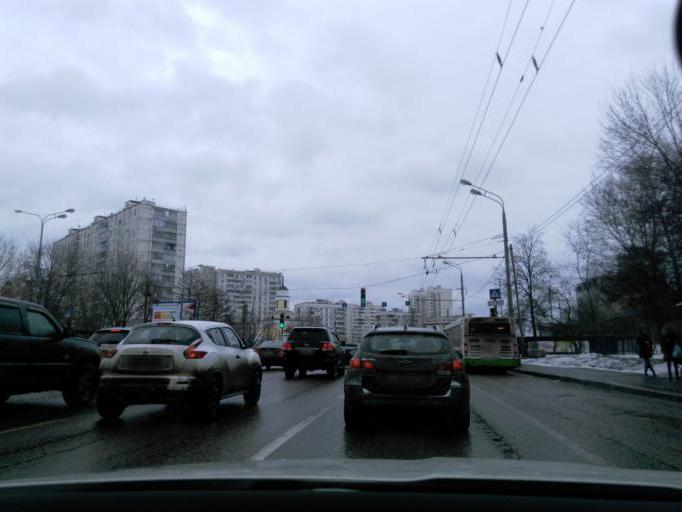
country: RU
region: Moscow
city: Likhobory
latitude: 55.8584
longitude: 37.5580
